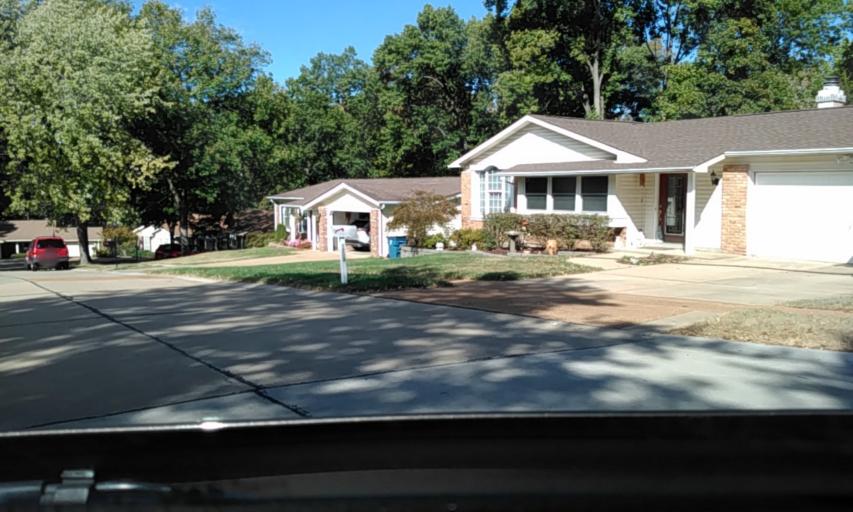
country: US
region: Missouri
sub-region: Jefferson County
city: Arnold
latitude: 38.4789
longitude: -90.3734
